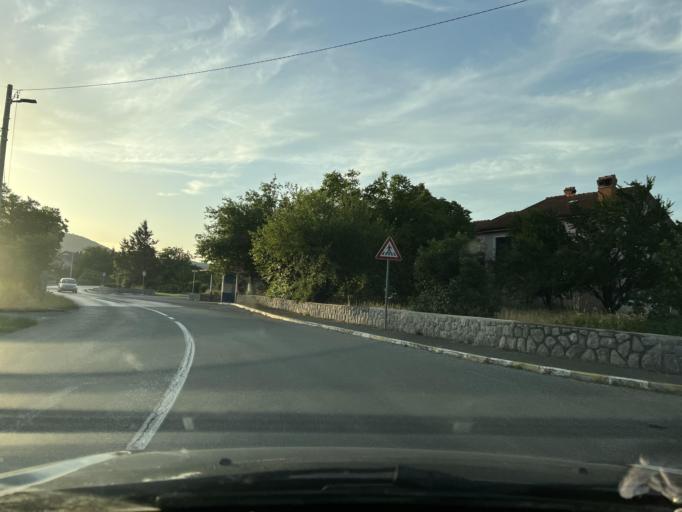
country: HR
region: Primorsko-Goranska
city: Drazice
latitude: 45.3841
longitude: 14.4707
